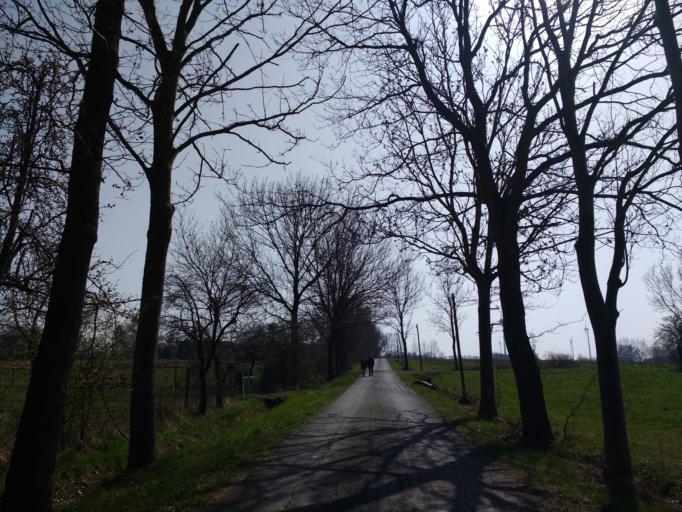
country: DE
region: North Rhine-Westphalia
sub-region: Regierungsbezirk Detmold
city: Salzkotten
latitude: 51.7276
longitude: 8.6515
